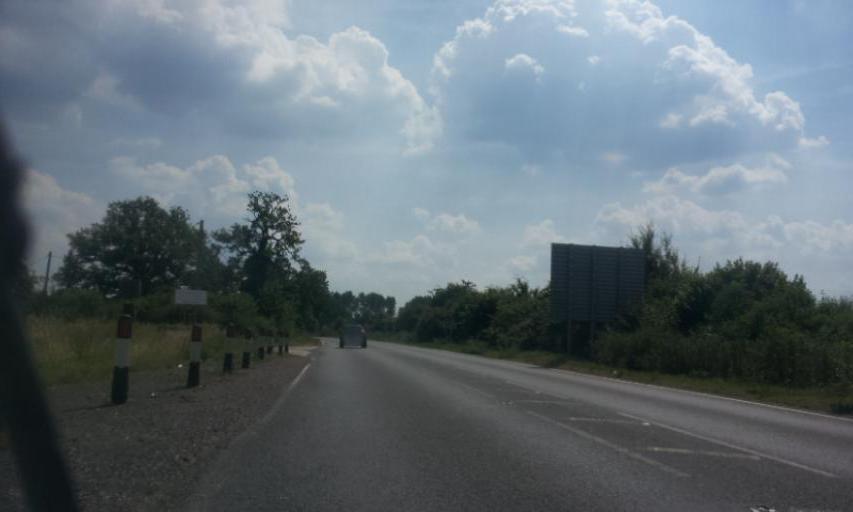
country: GB
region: England
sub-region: Kent
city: East Peckham
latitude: 51.1981
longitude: 0.3947
